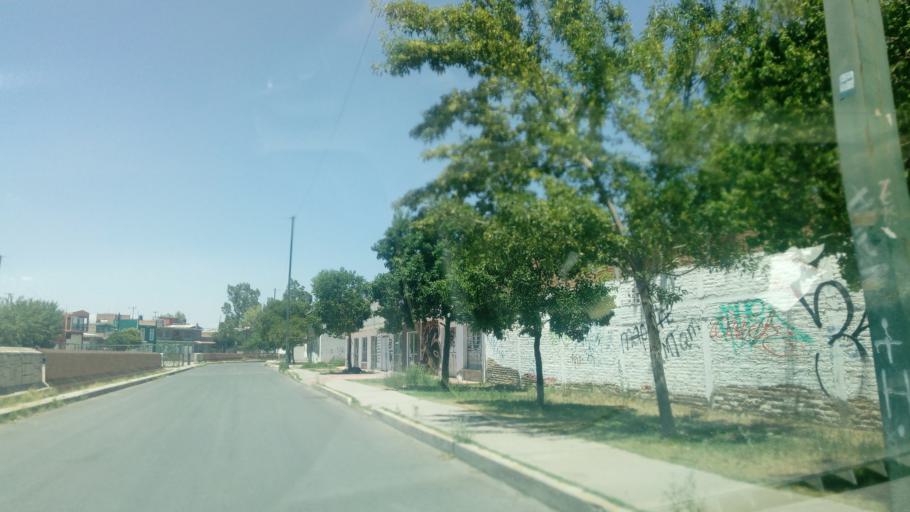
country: MX
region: Durango
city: Victoria de Durango
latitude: 24.0173
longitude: -104.6374
